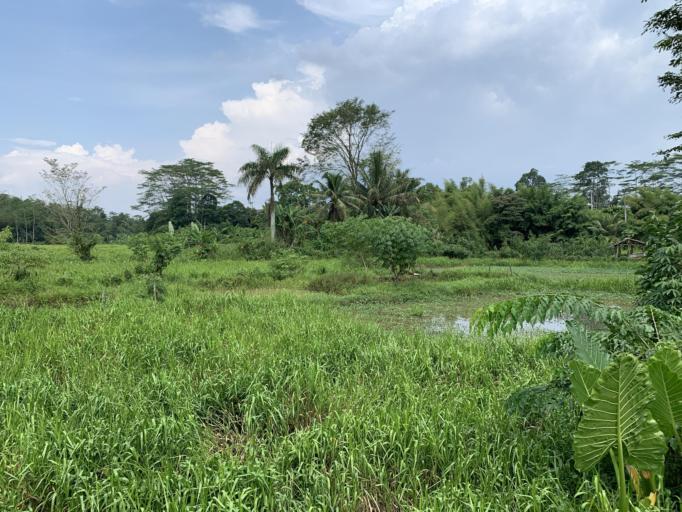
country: ID
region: West Java
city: Serpong
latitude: -6.4024
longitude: 106.6210
